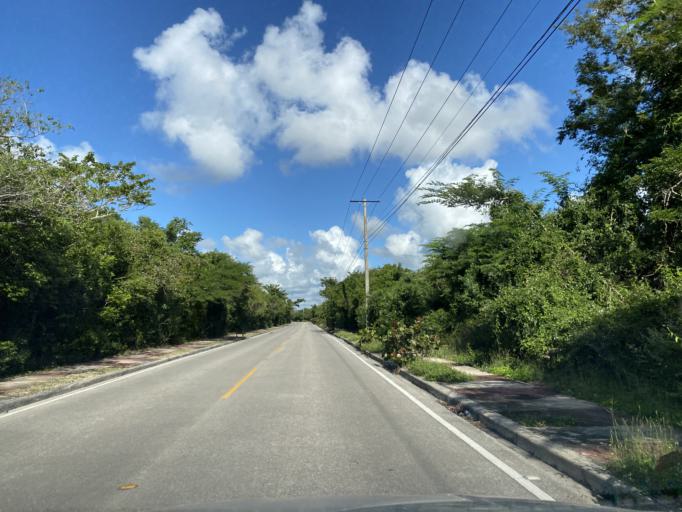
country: DO
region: La Altagracia
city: San Rafael del Yuma
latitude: 18.3391
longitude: -68.8115
